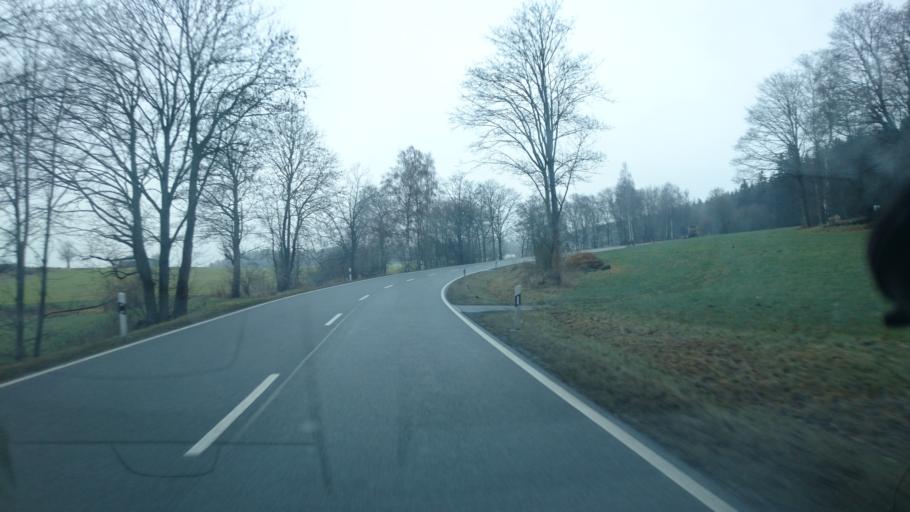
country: DE
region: Bavaria
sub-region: Upper Franconia
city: Topen
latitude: 50.4063
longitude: 11.8605
